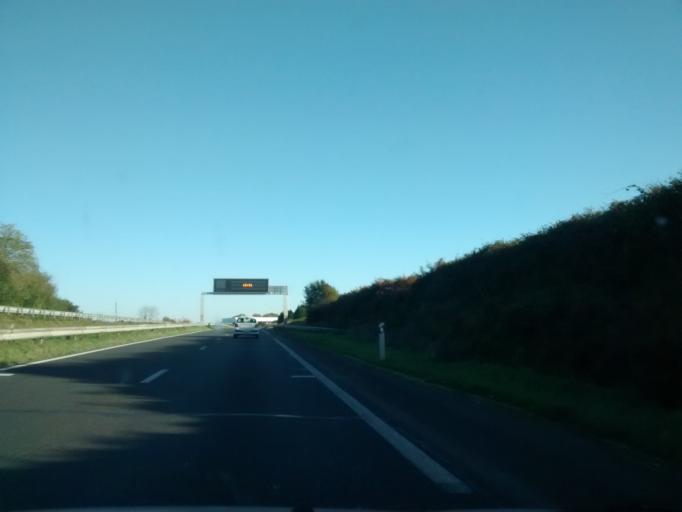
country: FR
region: Brittany
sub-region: Departement des Cotes-d'Armor
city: Tremuson
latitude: 48.5252
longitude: -2.8919
